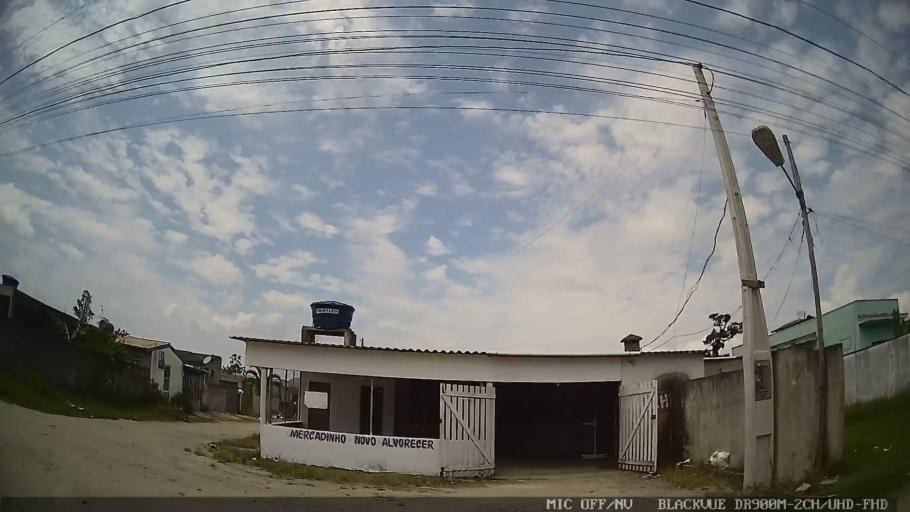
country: BR
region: Sao Paulo
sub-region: Caraguatatuba
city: Caraguatatuba
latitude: -23.6691
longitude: -45.4564
